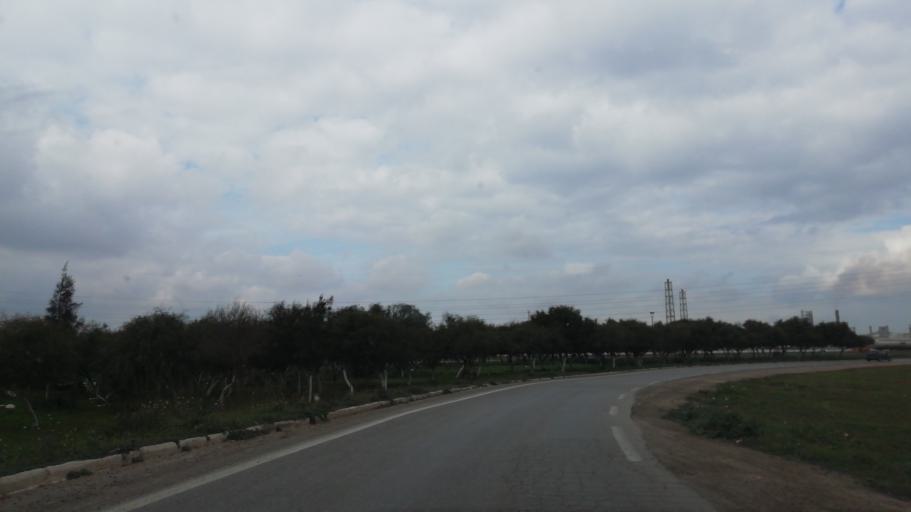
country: DZ
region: Oran
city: Ain el Bya
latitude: 35.7983
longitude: -0.3442
